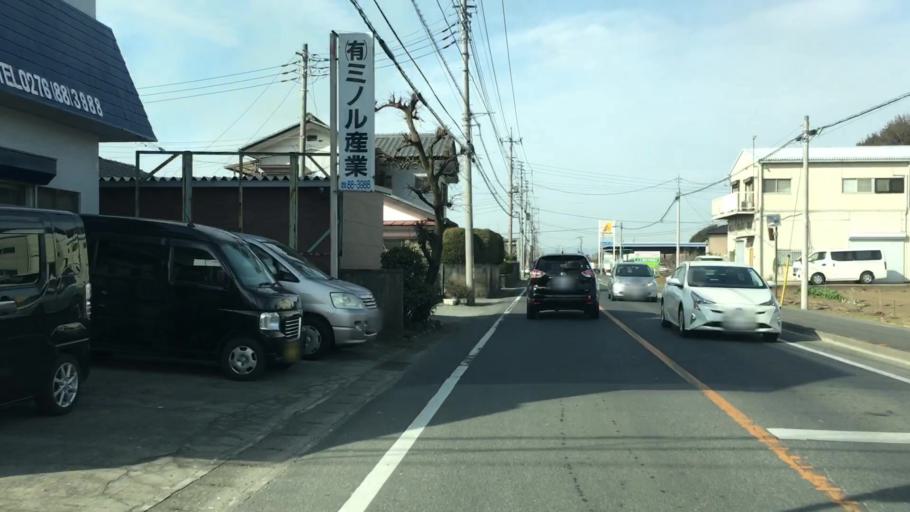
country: JP
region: Saitama
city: Menuma
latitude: 36.2418
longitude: 139.4514
